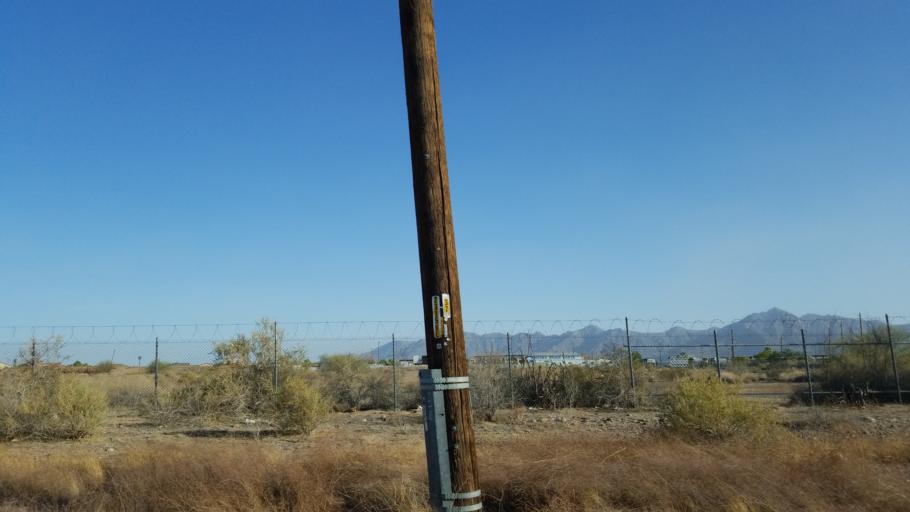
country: US
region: Arizona
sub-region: Maricopa County
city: Laveen
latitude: 33.3919
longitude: -112.2193
